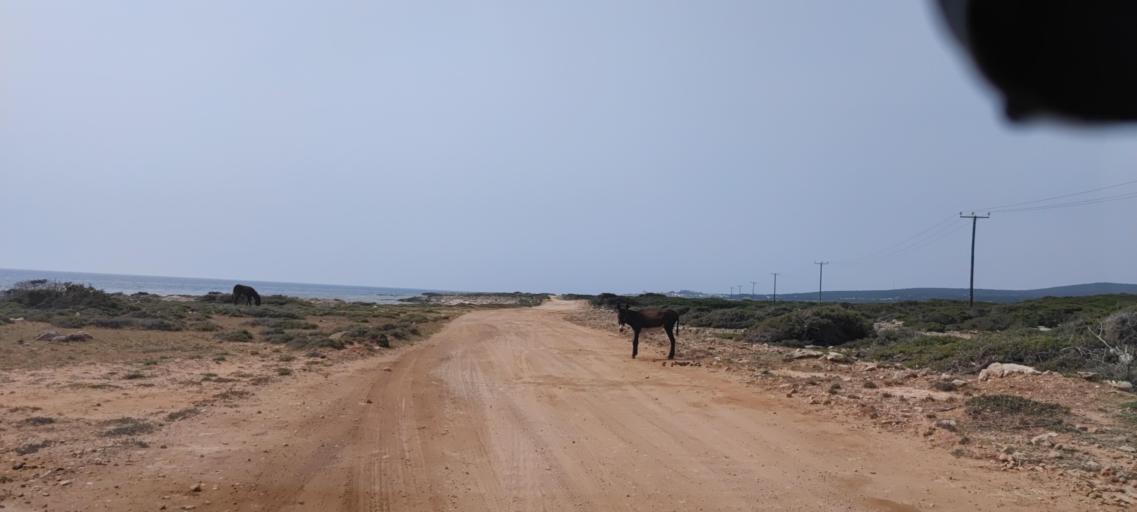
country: CY
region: Ammochostos
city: Rizokarpaso
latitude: 35.6774
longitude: 34.5778
